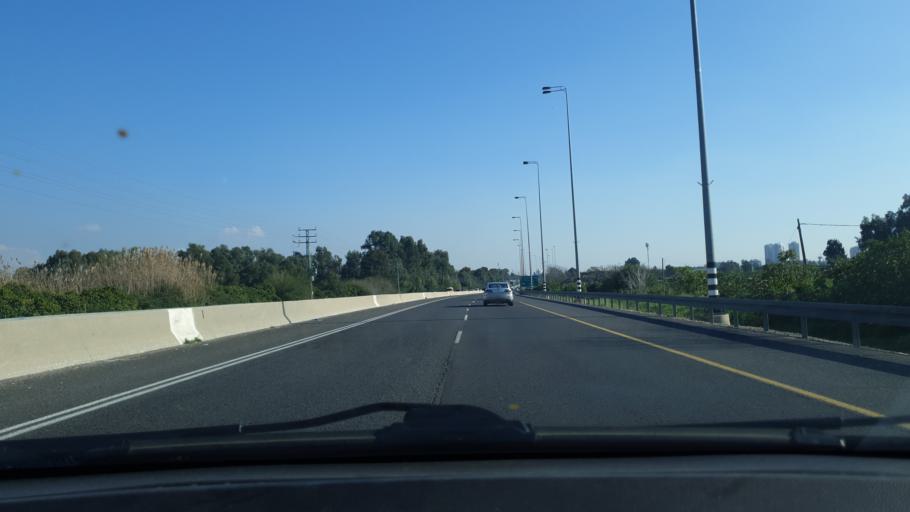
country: IL
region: Central District
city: Kefar Habad
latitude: 31.9576
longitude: 34.8532
